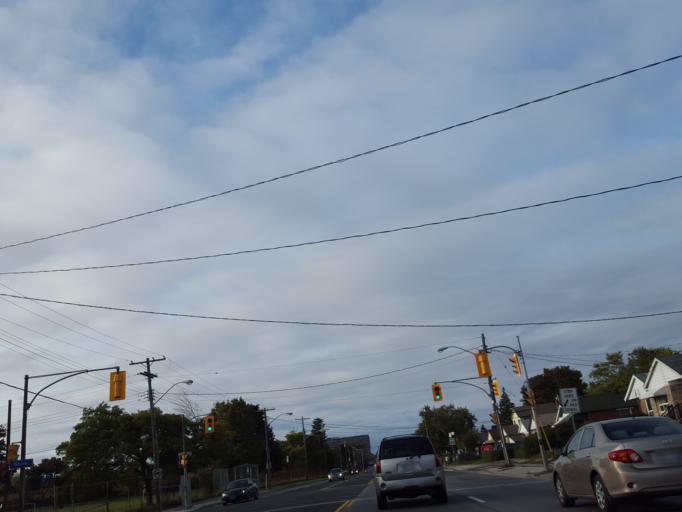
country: CA
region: Ontario
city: Scarborough
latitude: 43.7376
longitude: -79.2915
